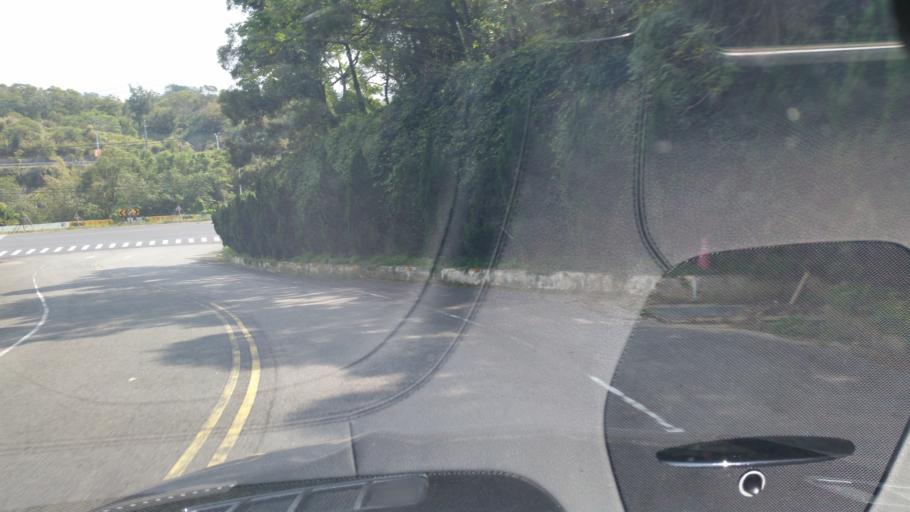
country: TW
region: Taiwan
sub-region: Miaoli
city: Miaoli
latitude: 24.6248
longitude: 120.8462
